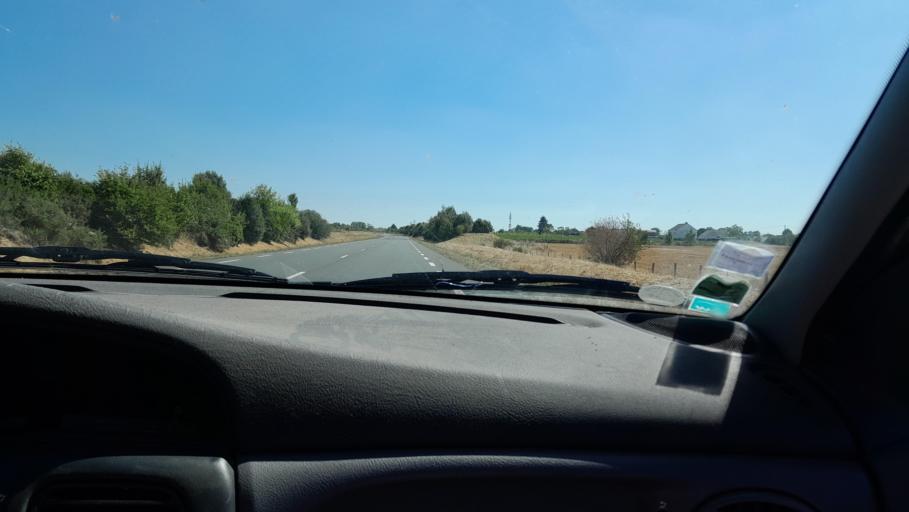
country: FR
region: Pays de la Loire
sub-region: Departement de la Loire-Atlantique
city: Saint-Gereon
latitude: 47.3774
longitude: -1.2126
